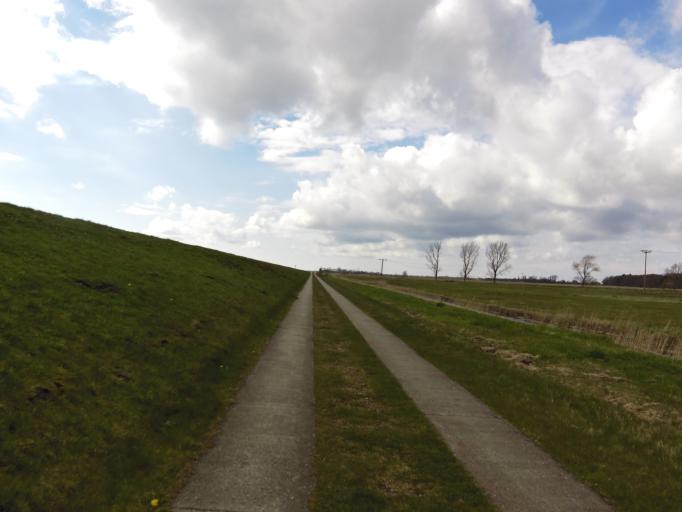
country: DE
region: Mecklenburg-Vorpommern
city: Barth
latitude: 54.4149
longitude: 12.7551
